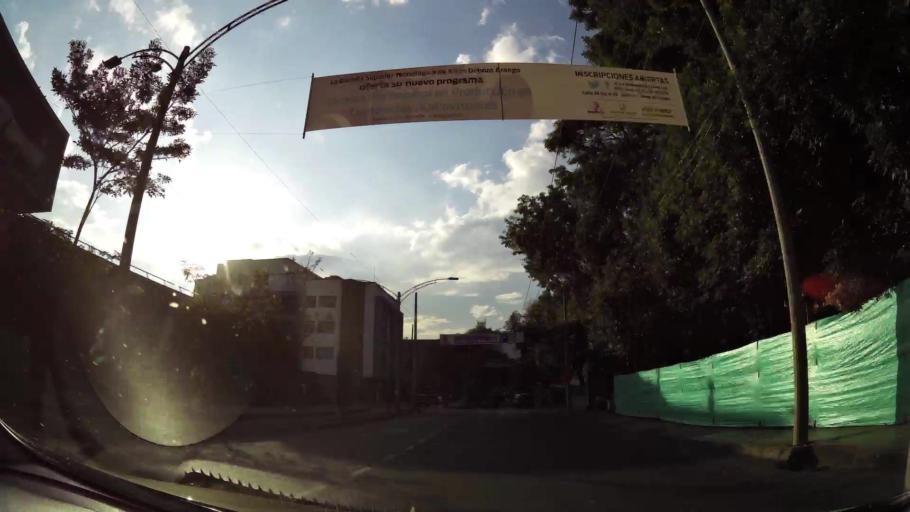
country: CO
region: Antioquia
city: Envigado
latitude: 6.1726
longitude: -75.5906
